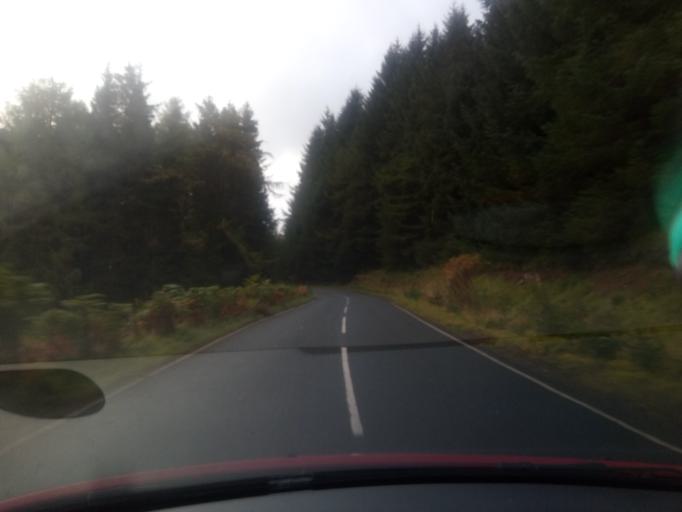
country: GB
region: Scotland
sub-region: The Scottish Borders
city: Hawick
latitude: 55.3364
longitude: -2.6501
